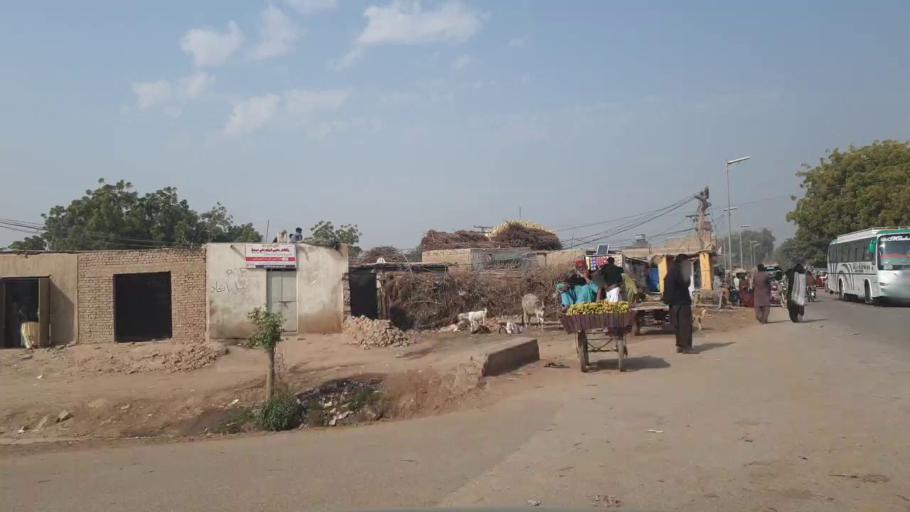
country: PK
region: Sindh
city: Hala
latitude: 25.8114
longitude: 68.4354
